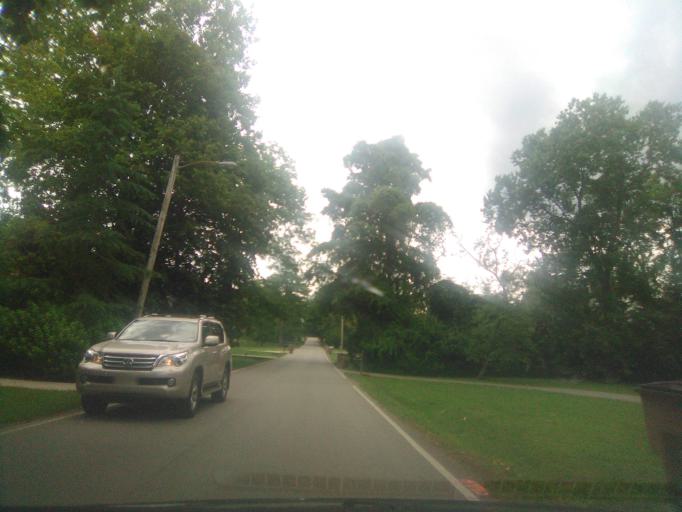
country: US
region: Tennessee
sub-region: Davidson County
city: Belle Meade
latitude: 36.0891
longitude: -86.8697
